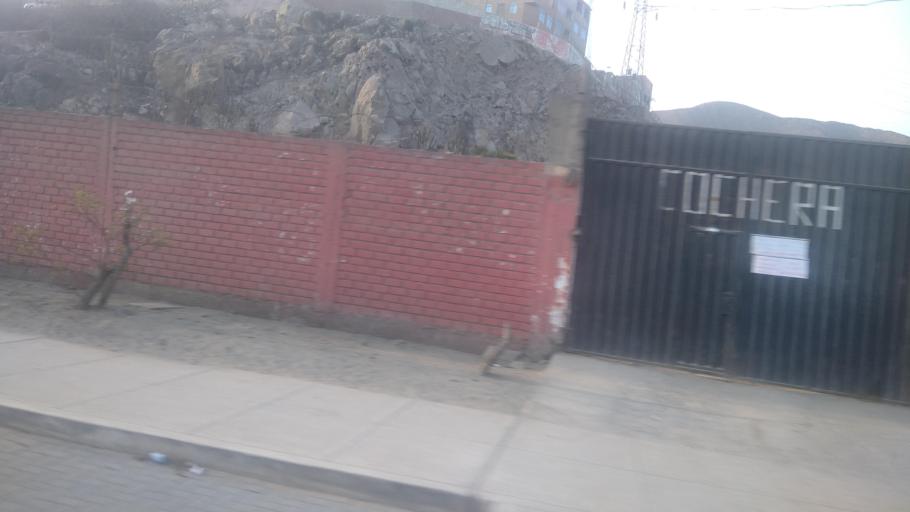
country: PE
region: Lima
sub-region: Lima
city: Vitarte
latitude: -12.0246
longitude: -76.9793
